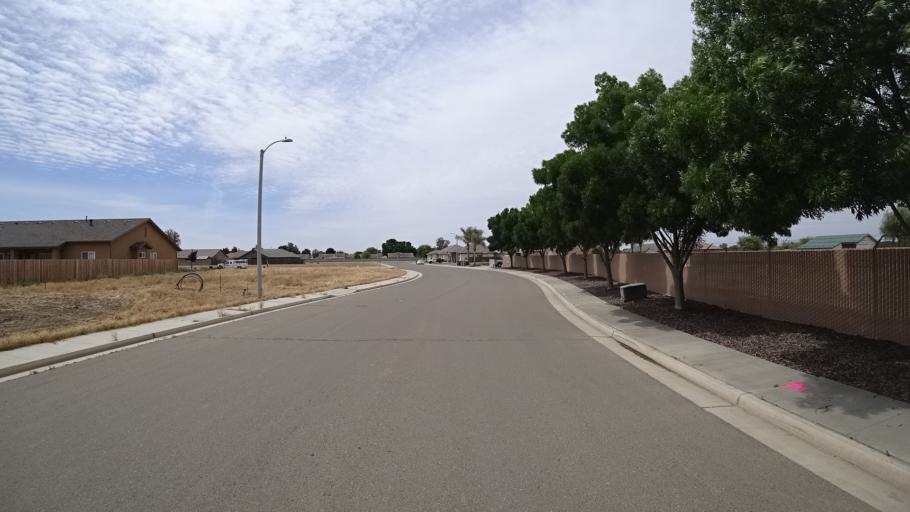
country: US
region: California
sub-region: Kings County
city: Lucerne
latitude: 36.3709
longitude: -119.6386
